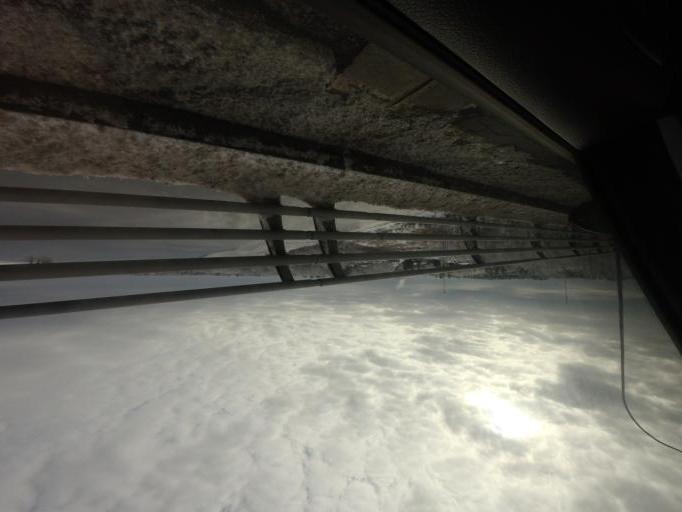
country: CA
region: New Brunswick
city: Oromocto
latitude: 45.8631
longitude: -66.4500
